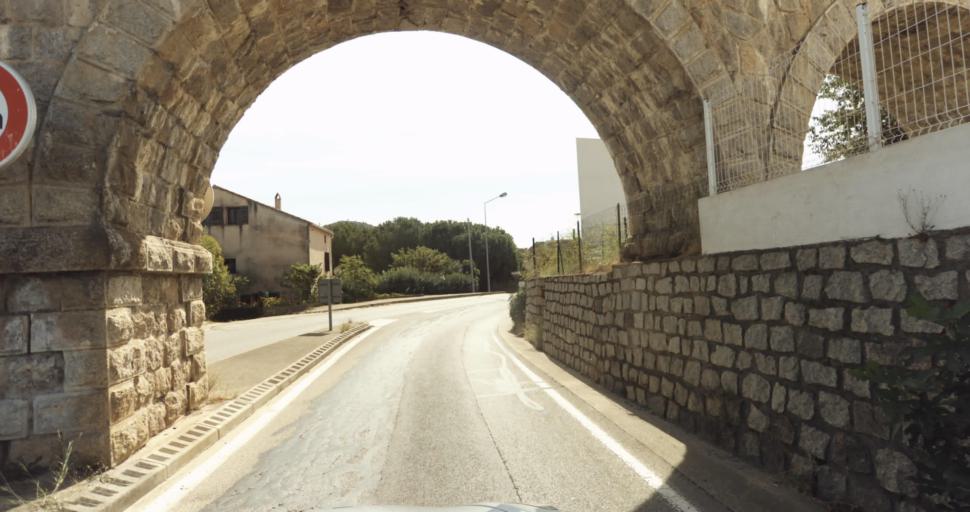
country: FR
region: Corsica
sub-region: Departement de la Corse-du-Sud
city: Afa
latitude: 41.9537
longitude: 8.7840
